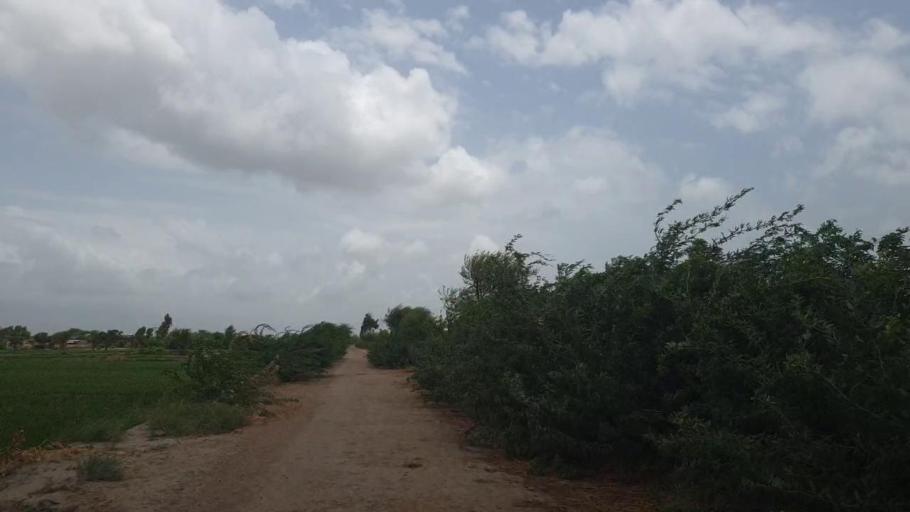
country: PK
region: Sindh
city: Badin
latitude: 24.6641
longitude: 68.8925
